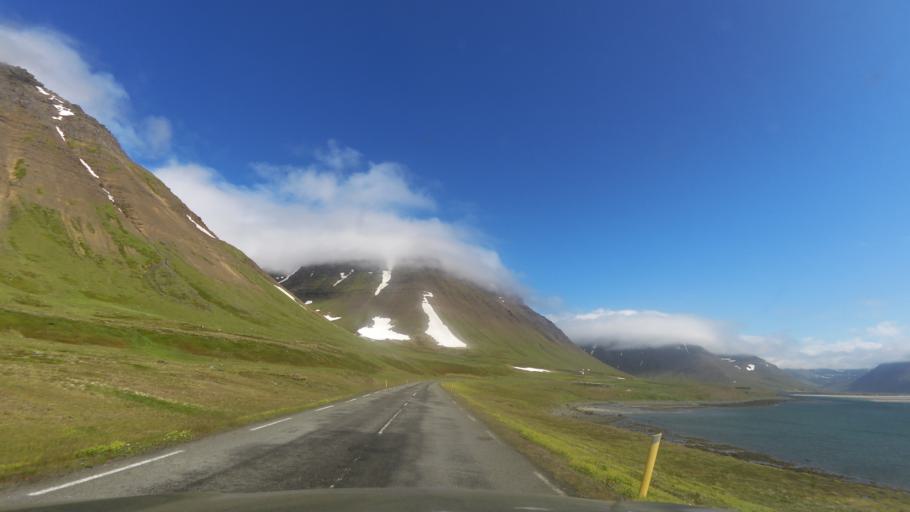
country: IS
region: Westfjords
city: Isafjoerdur
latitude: 66.0410
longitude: -23.4544
